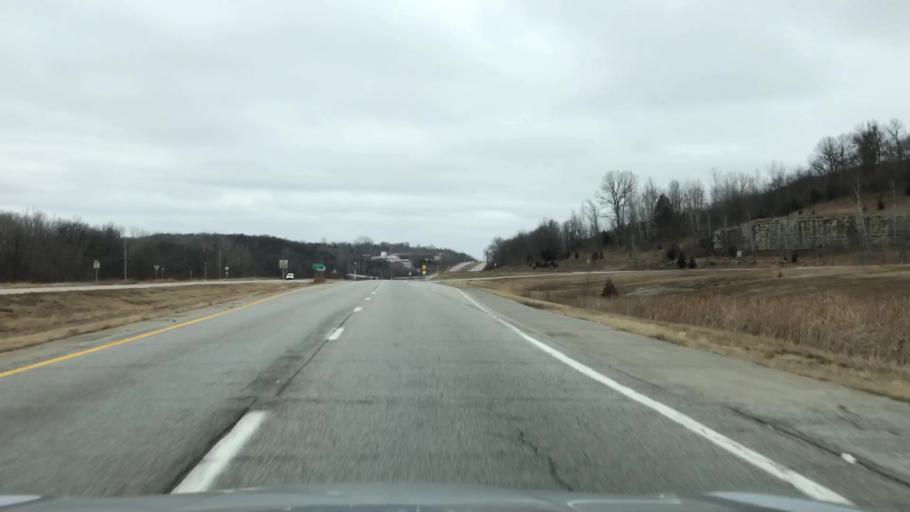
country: US
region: Missouri
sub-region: Jackson County
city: East Independence
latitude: 39.1392
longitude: -94.3873
